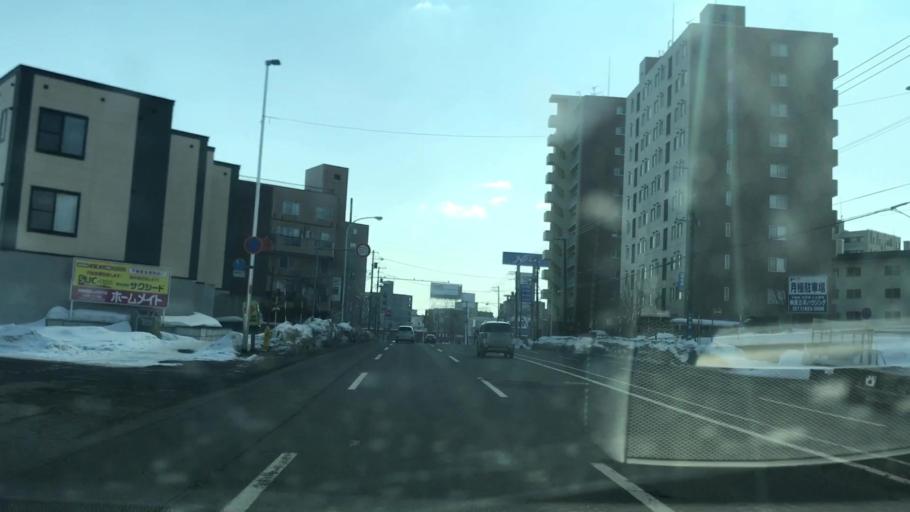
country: JP
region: Hokkaido
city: Sapporo
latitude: 43.0326
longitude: 141.3623
